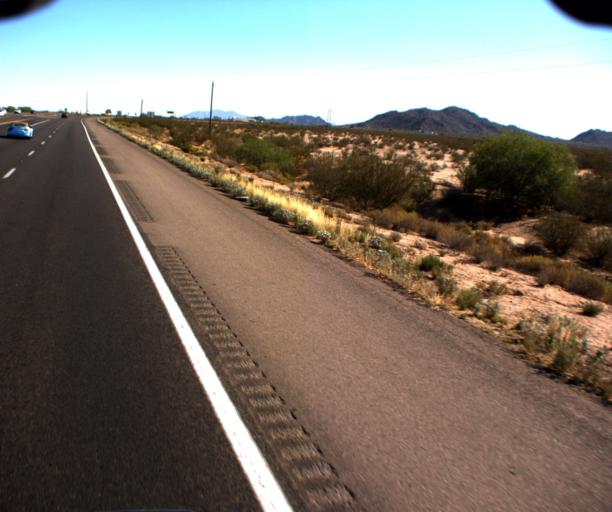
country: US
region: Arizona
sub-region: Pinal County
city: Sacaton
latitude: 32.9914
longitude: -111.7567
